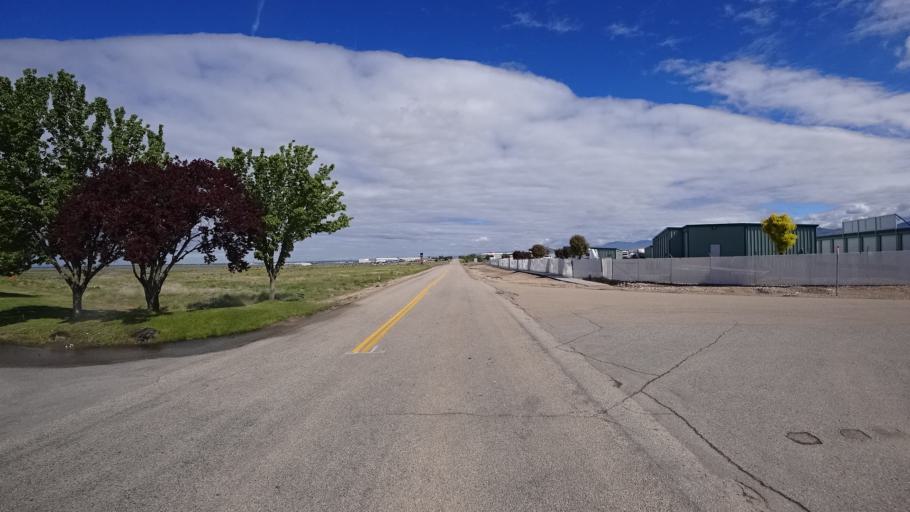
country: US
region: Idaho
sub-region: Ada County
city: Boise
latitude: 43.5277
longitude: -116.1556
